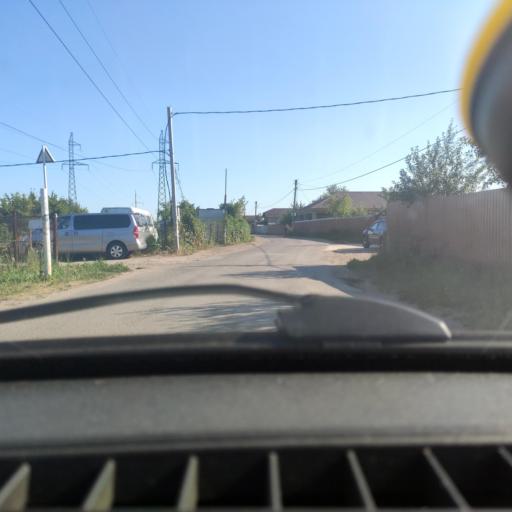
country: RU
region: Samara
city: Tol'yatti
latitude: 53.5824
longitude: 49.3000
